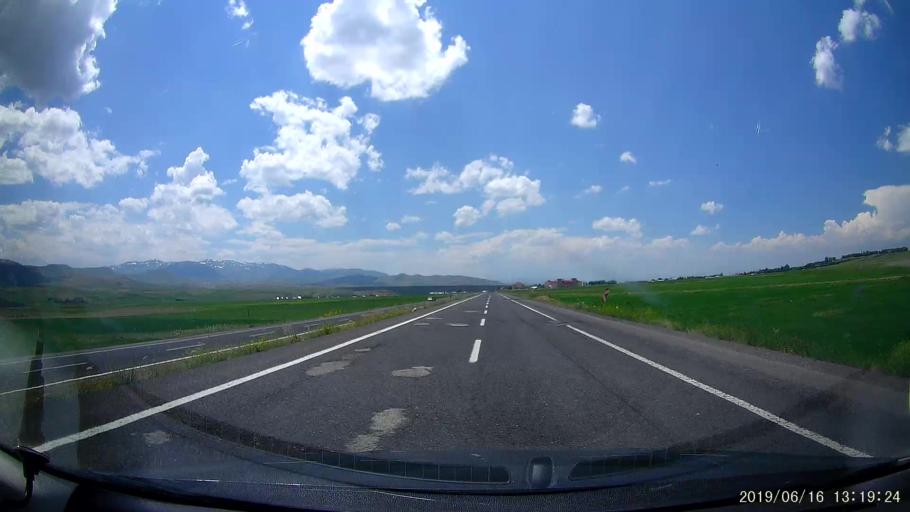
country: TR
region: Agri
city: Taslicay
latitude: 39.6328
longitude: 43.4078
